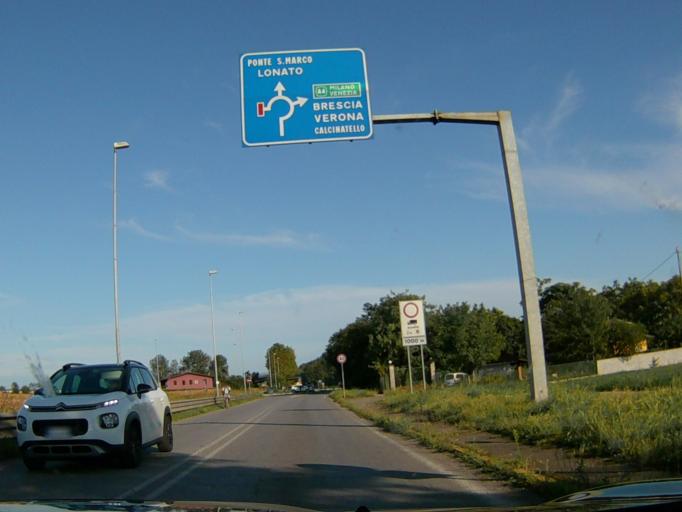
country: IT
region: Lombardy
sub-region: Provincia di Brescia
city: Molinetto
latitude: 45.4857
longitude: 10.3729
